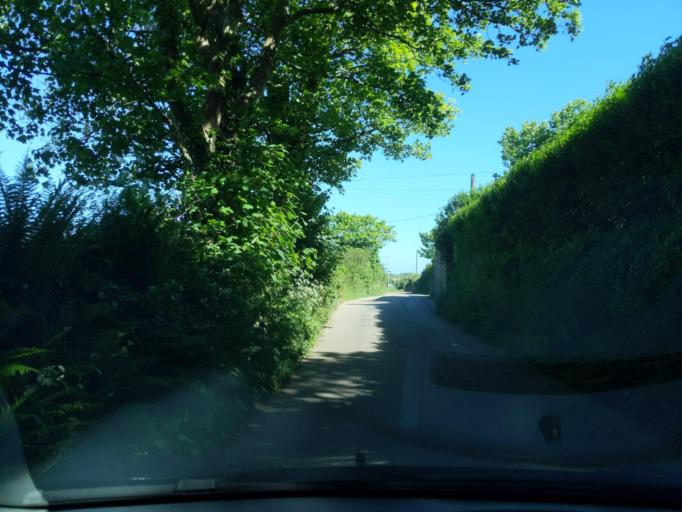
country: GB
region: England
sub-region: Cornwall
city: St. Buryan
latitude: 50.0738
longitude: -5.6188
